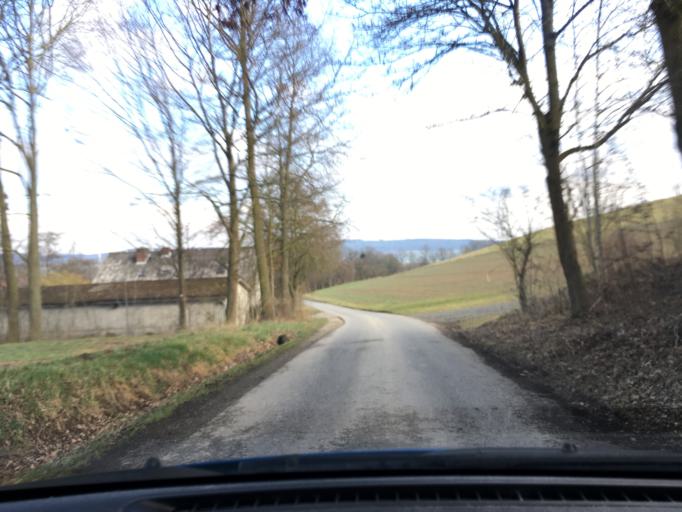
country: DE
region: Lower Saxony
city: Uslar
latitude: 51.6437
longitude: 9.6324
